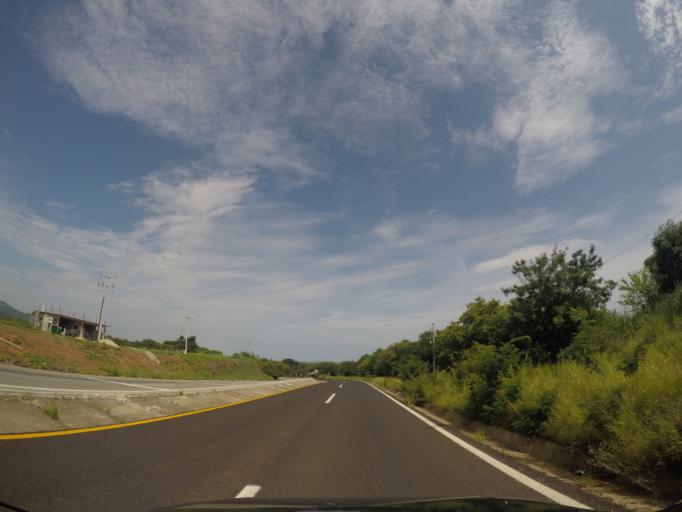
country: MX
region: Oaxaca
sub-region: Santa Maria Colotepec
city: Brisas de Zicatela
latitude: 15.8173
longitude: -97.0121
